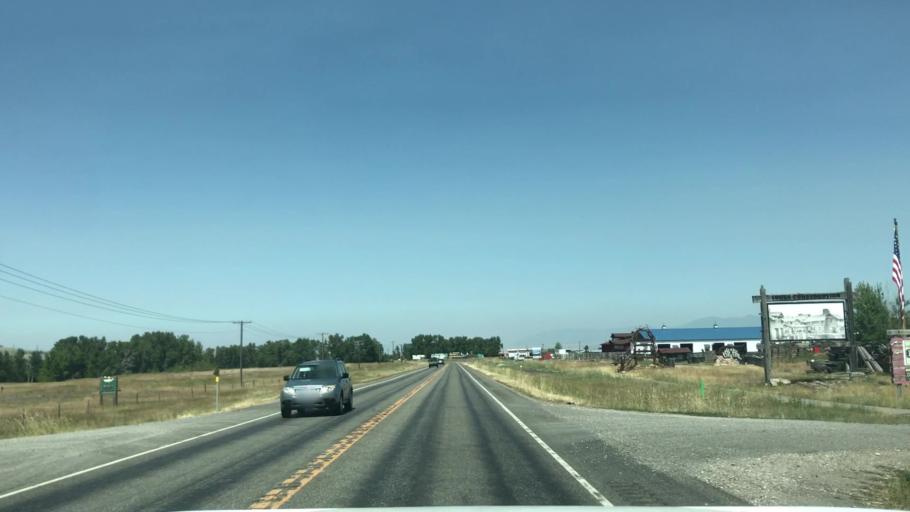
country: US
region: Montana
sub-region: Gallatin County
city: Four Corners
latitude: 45.6037
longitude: -111.1960
